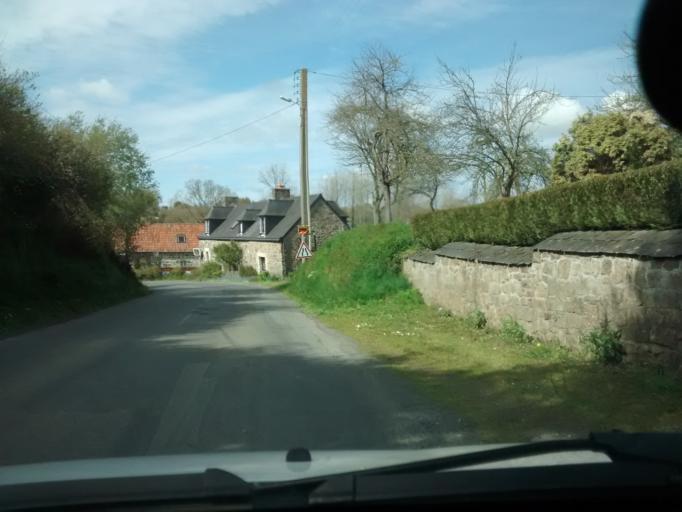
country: FR
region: Brittany
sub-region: Departement des Cotes-d'Armor
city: Langoat
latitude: 48.7739
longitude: -3.2810
